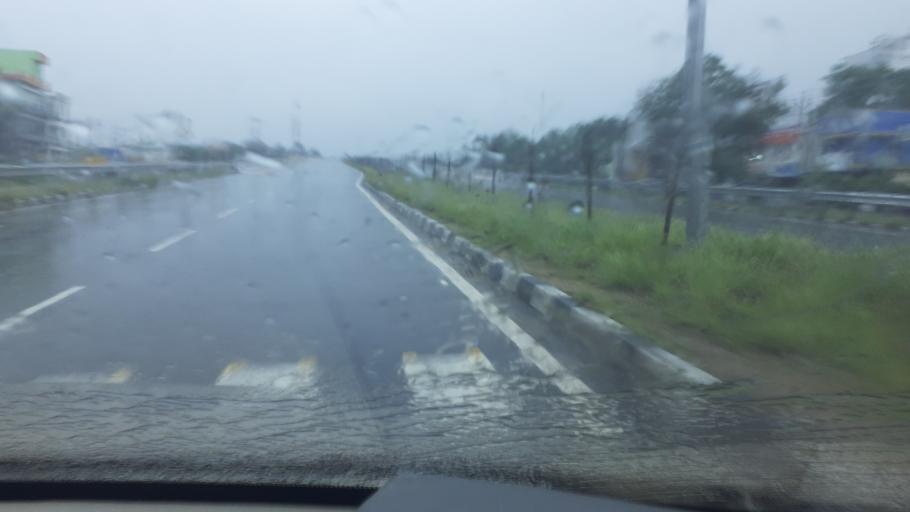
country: IN
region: Tamil Nadu
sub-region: Virudhunagar
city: Virudunagar
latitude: 9.6045
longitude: 77.9550
